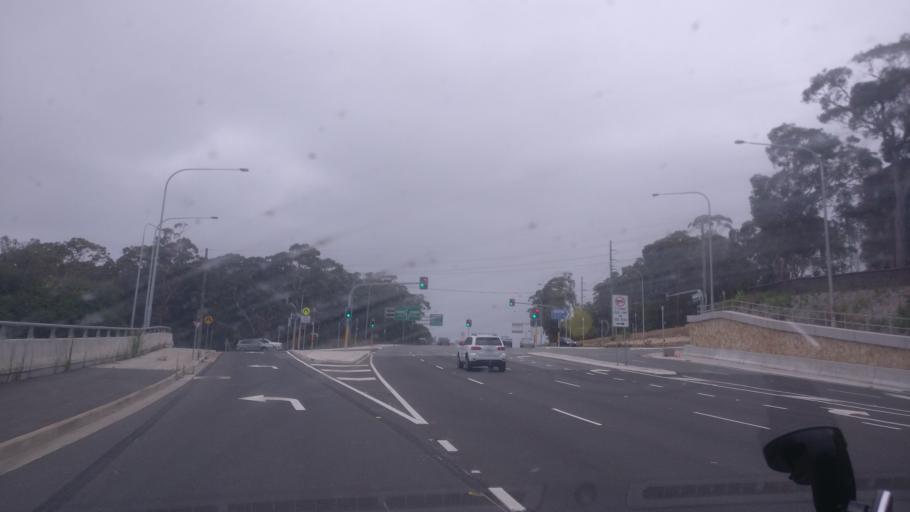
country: AU
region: New South Wales
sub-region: Warringah
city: Allambie Heights
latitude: -33.7492
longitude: 151.2350
